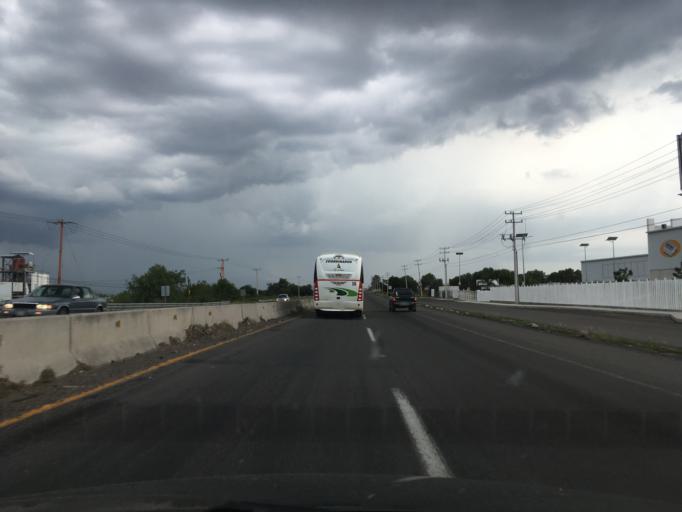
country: MX
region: Guanajuato
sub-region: Celaya
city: El Sauz (El Sauz de Villasenor)
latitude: 20.3975
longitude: -100.7889
